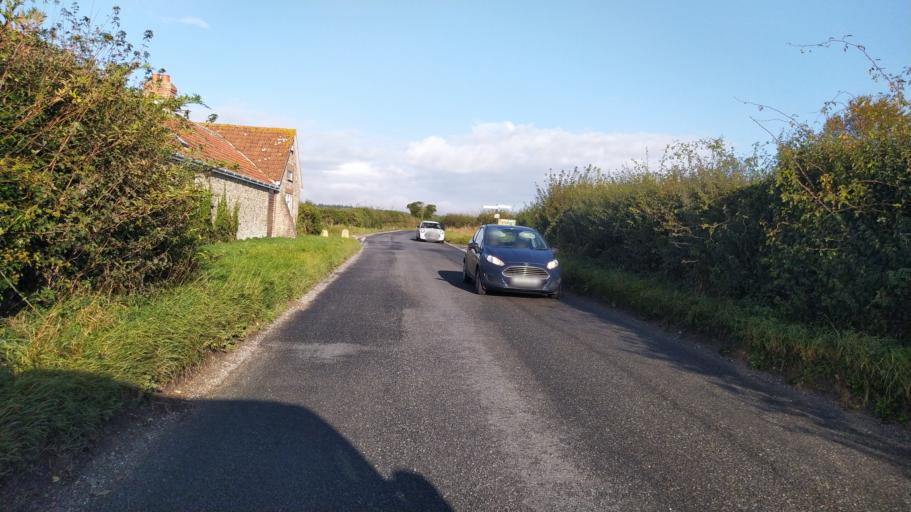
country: GB
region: England
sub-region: Wiltshire
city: Ansty
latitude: 50.9316
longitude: -2.0634
